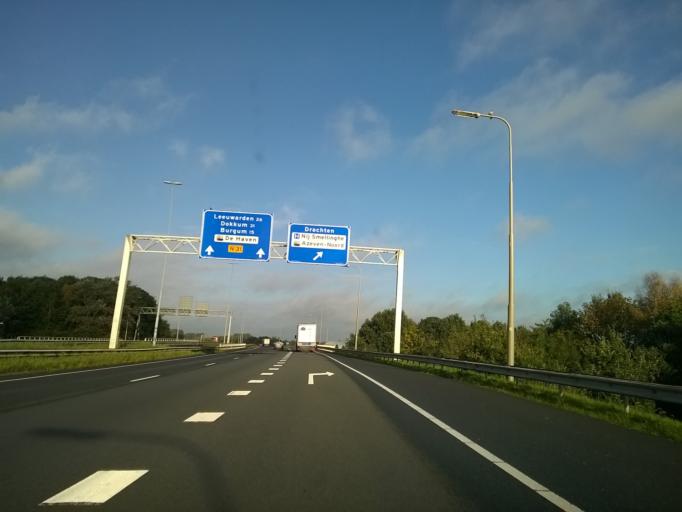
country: NL
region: Friesland
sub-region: Gemeente Smallingerland
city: Drachtstercompagnie
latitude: 53.1079
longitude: 6.1317
